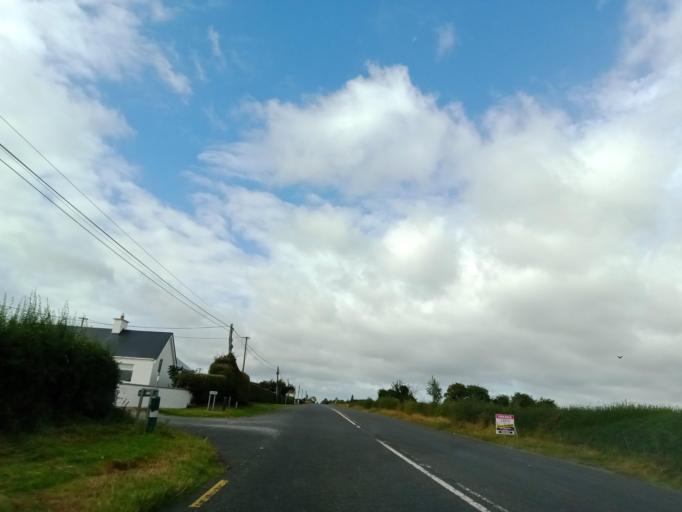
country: IE
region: Leinster
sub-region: Laois
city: Abbeyleix
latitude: 52.8291
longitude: -7.4549
